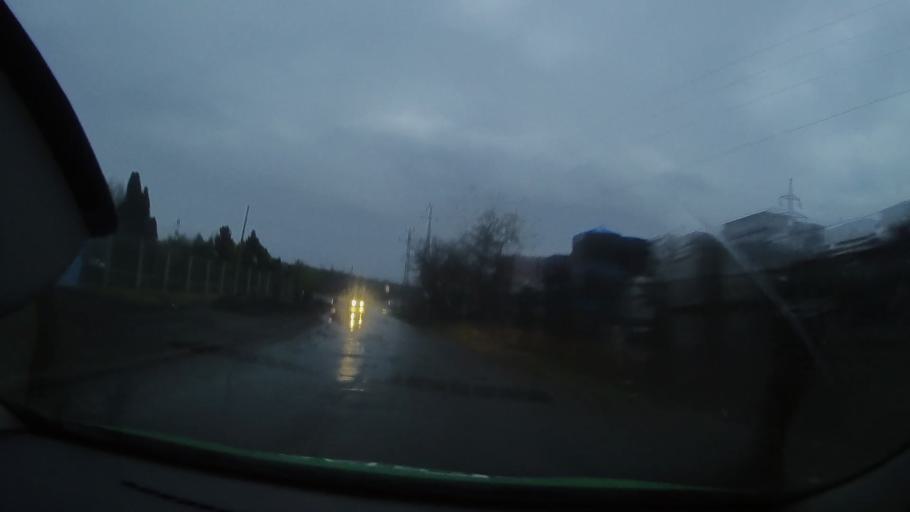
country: RO
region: Mures
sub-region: Municipiul Reghin
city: Iernuteni
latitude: 46.7666
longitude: 24.7223
